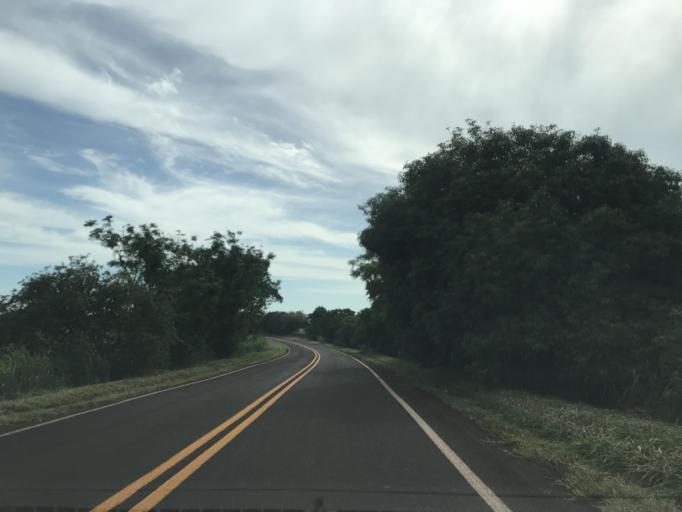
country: BR
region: Parana
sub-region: Terra Rica
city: Terra Rica
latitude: -22.7713
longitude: -52.6462
